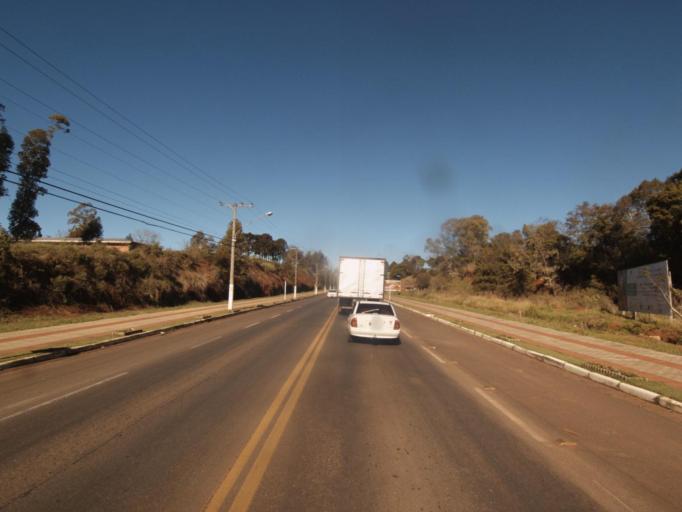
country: AR
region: Misiones
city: Bernardo de Irigoyen
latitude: -26.7565
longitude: -53.5053
